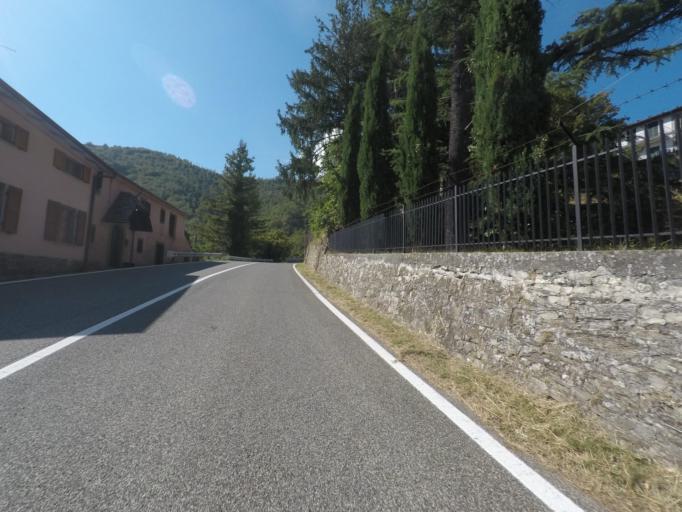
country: IT
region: Tuscany
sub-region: Provincia di Massa-Carrara
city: Fivizzano
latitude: 44.2569
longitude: 10.1728
